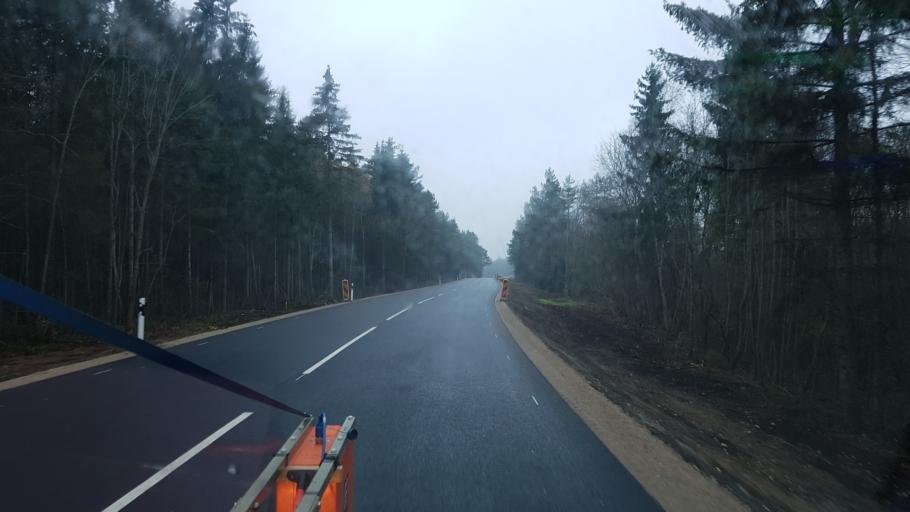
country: EE
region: Raplamaa
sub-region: Kohila vald
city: Kohila
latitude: 59.1781
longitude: 24.7891
